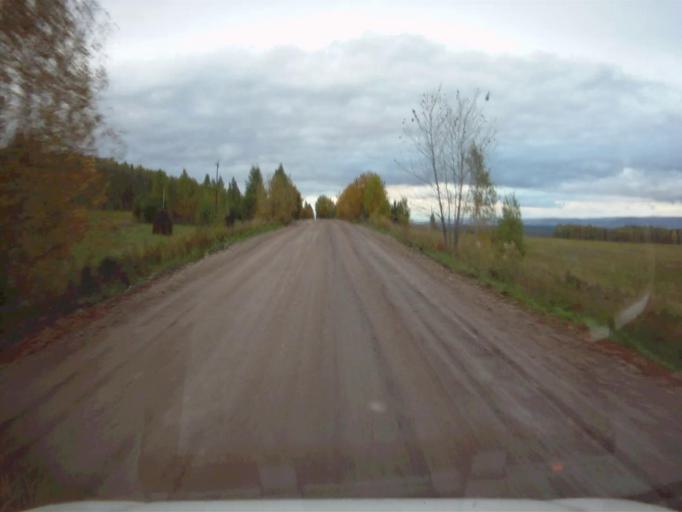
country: RU
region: Sverdlovsk
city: Mikhaylovsk
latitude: 56.1993
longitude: 59.2000
